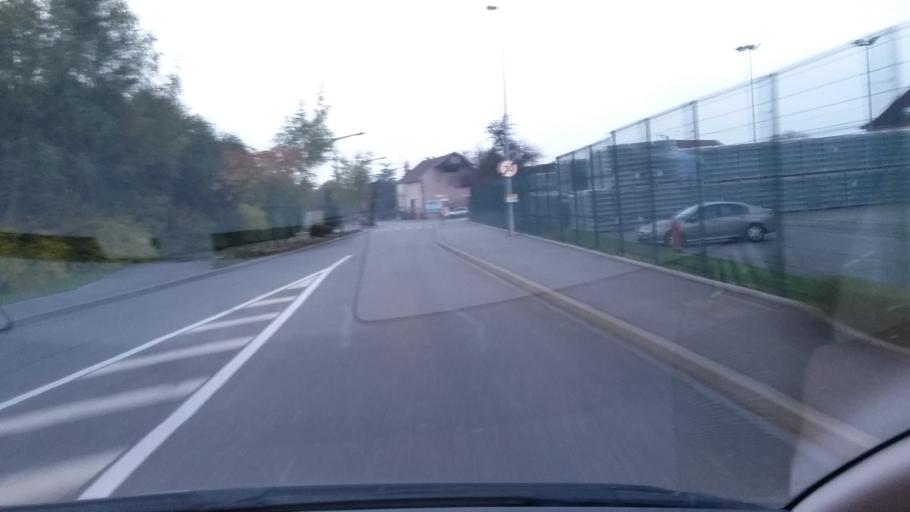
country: FR
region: Alsace
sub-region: Departement du Bas-Rhin
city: Drulingen
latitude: 48.8687
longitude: 7.2744
